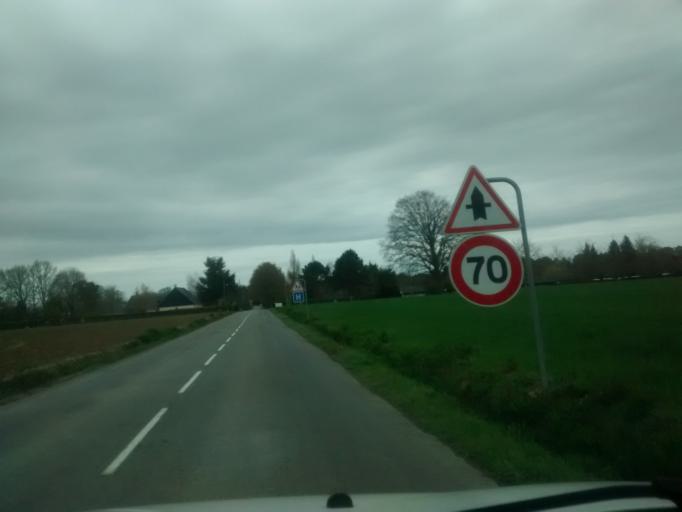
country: FR
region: Brittany
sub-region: Departement d'Ille-et-Vilaine
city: Fouillard
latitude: 48.1729
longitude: -1.6012
